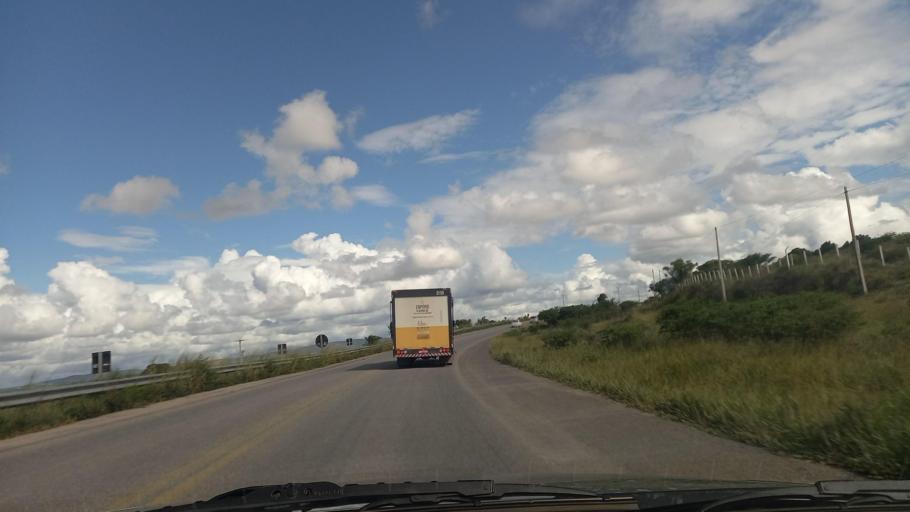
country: BR
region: Pernambuco
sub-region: Sao Joao
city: Sao Joao
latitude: -8.7717
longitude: -36.4270
